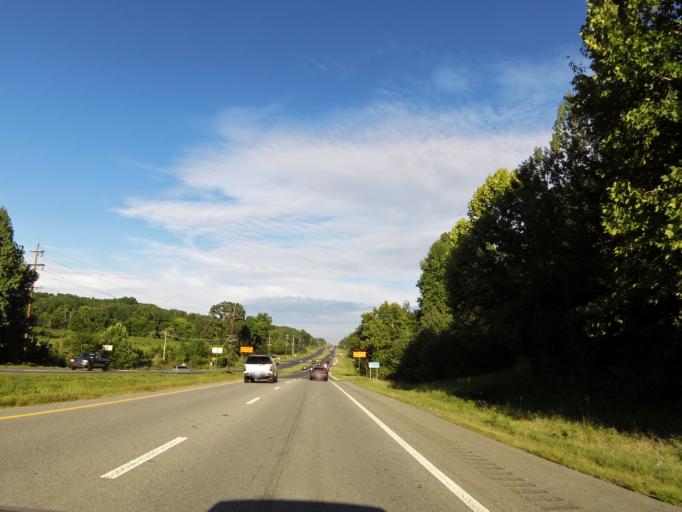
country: US
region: Alabama
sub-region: Lauderdale County
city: Killen
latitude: 34.8597
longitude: -87.5221
